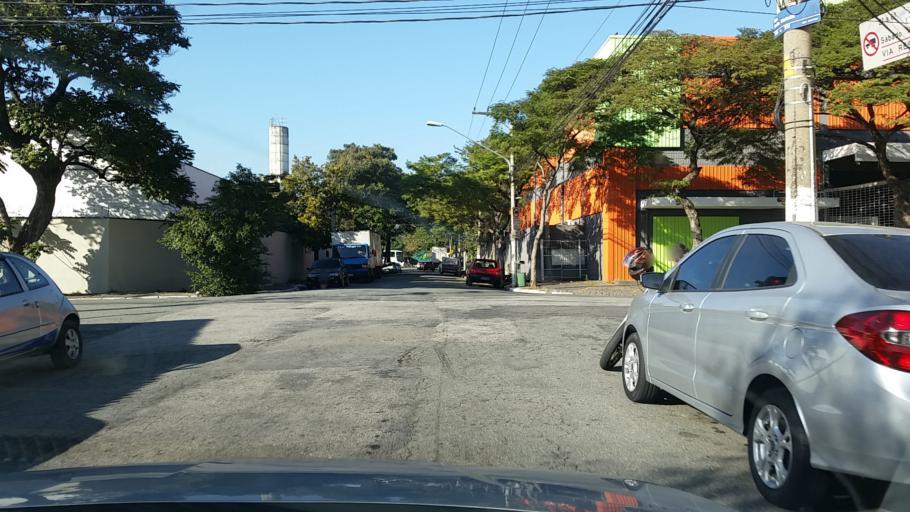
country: BR
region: Sao Paulo
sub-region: Sao Paulo
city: Sao Paulo
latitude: -23.5143
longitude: -46.6520
